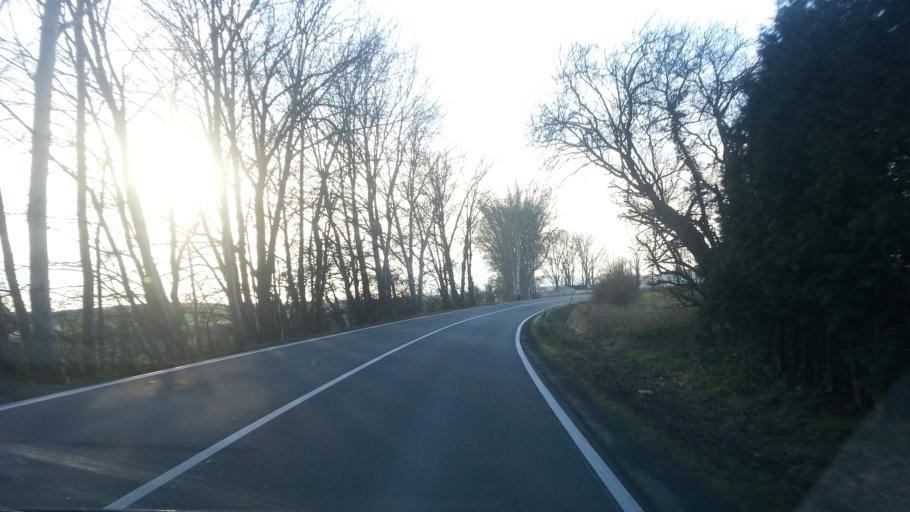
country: DE
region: Rheinland-Pfalz
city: Bischheim
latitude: 49.6682
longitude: 8.0352
